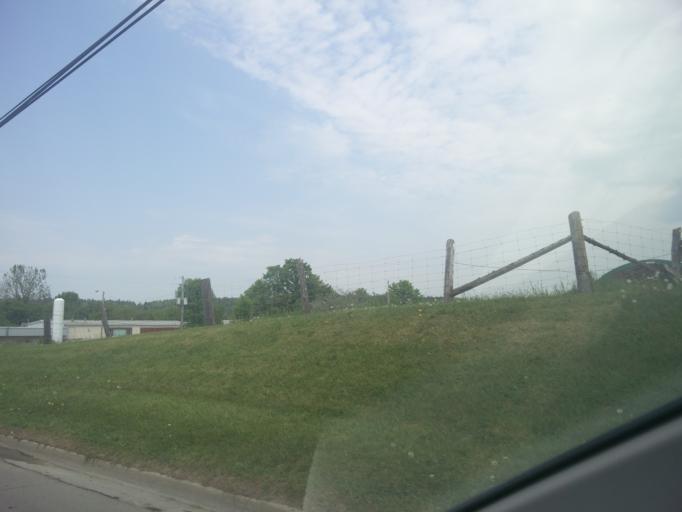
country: CA
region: Ontario
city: Perth
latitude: 44.6724
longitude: -76.3952
